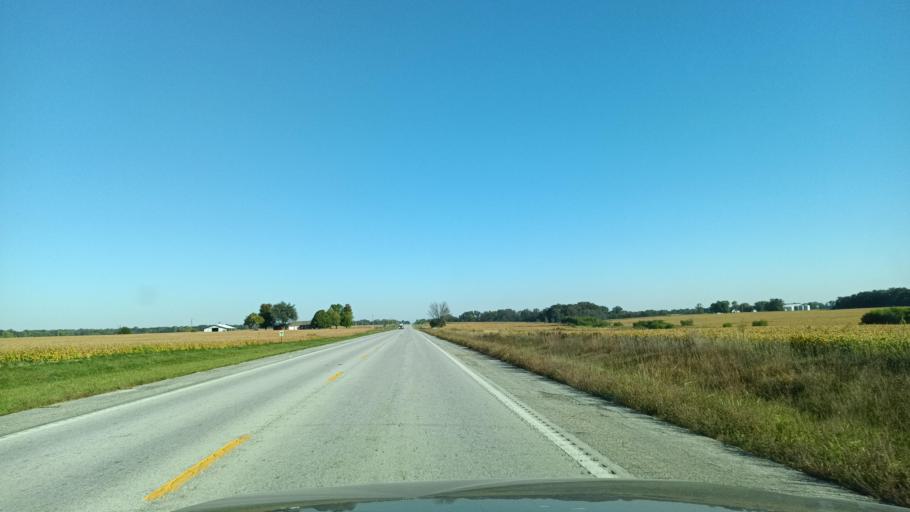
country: US
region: Missouri
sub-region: Audrain County
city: Vandalia
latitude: 39.2882
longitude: -91.6440
